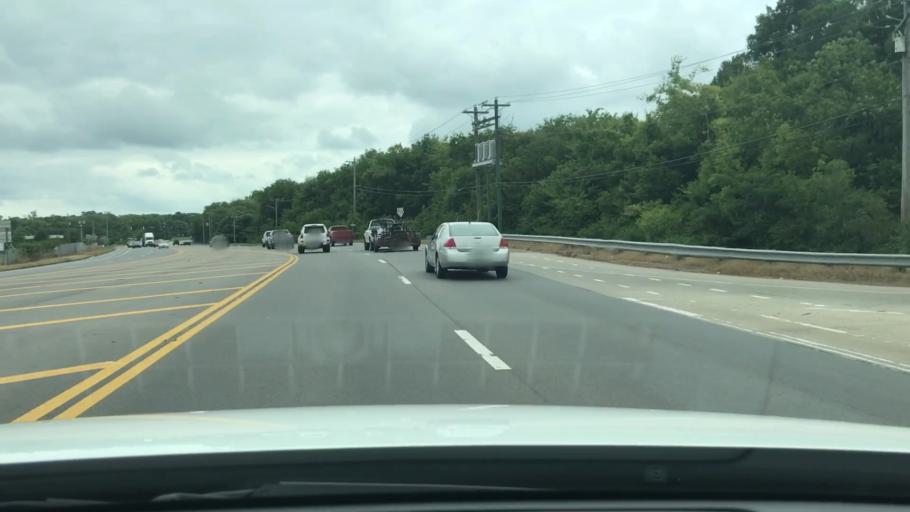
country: US
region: Tennessee
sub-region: Sumner County
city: Gallatin
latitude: 36.3869
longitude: -86.4763
